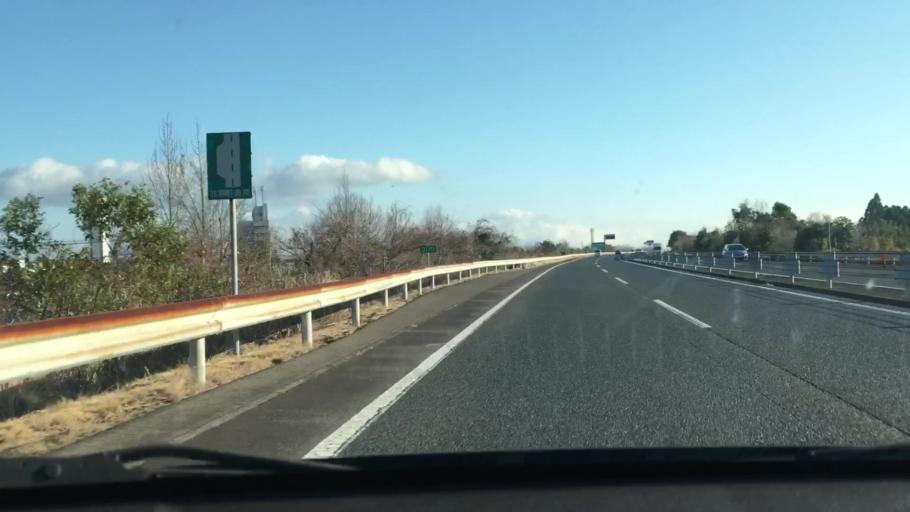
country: JP
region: Kagoshima
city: Kajiki
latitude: 31.7976
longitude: 130.7147
